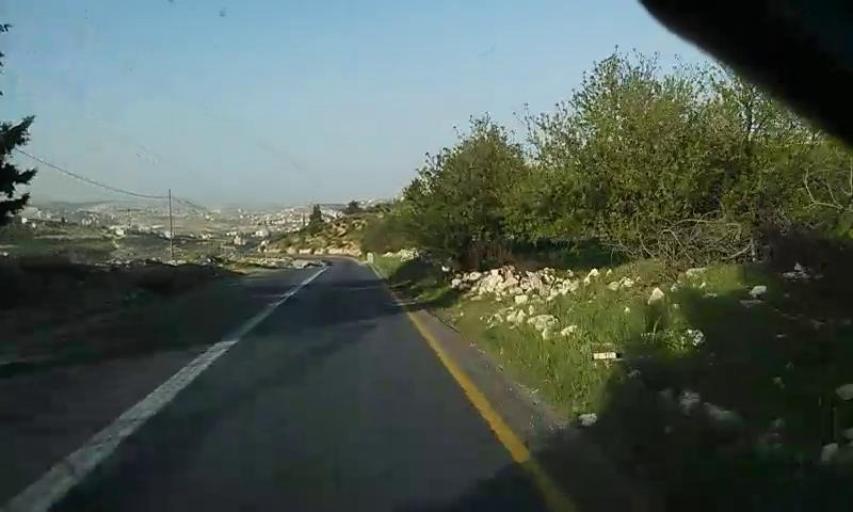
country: PS
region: West Bank
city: Marah Rabbah
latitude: 31.6477
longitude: 35.2034
